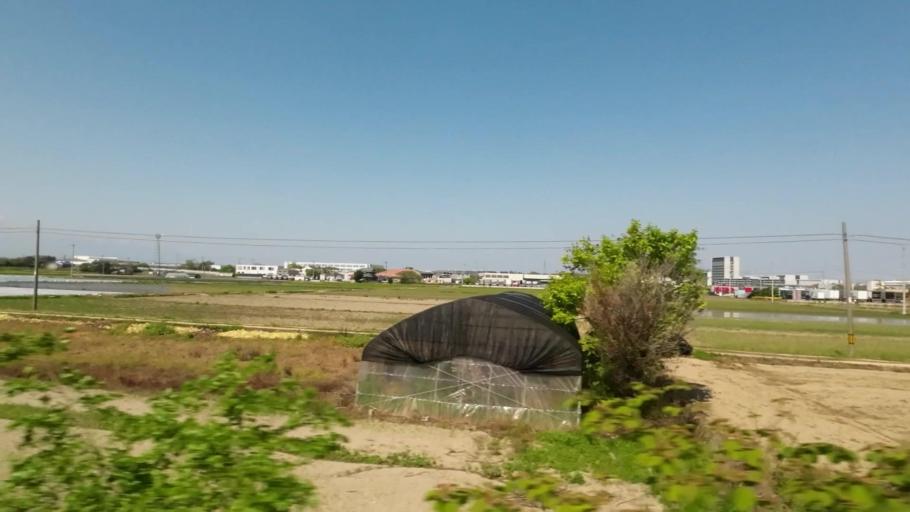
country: JP
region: Kagawa
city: Kan'onjicho
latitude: 34.1133
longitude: 133.6485
